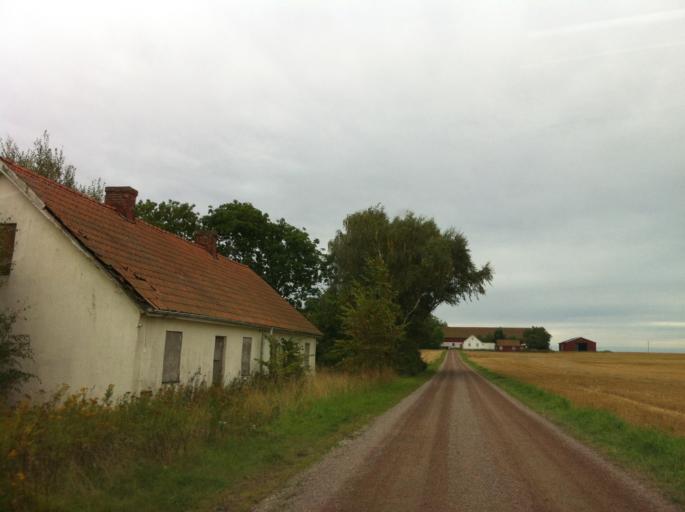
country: SE
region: Skane
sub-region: Landskrona
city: Asmundtorp
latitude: 55.9420
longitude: 12.9949
